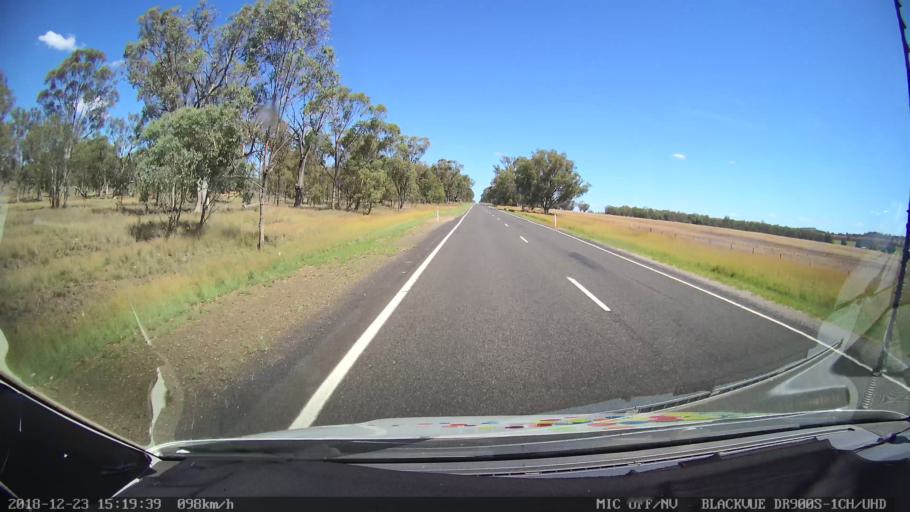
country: AU
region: New South Wales
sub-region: Tamworth Municipality
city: Manilla
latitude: -30.8318
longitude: 150.7842
